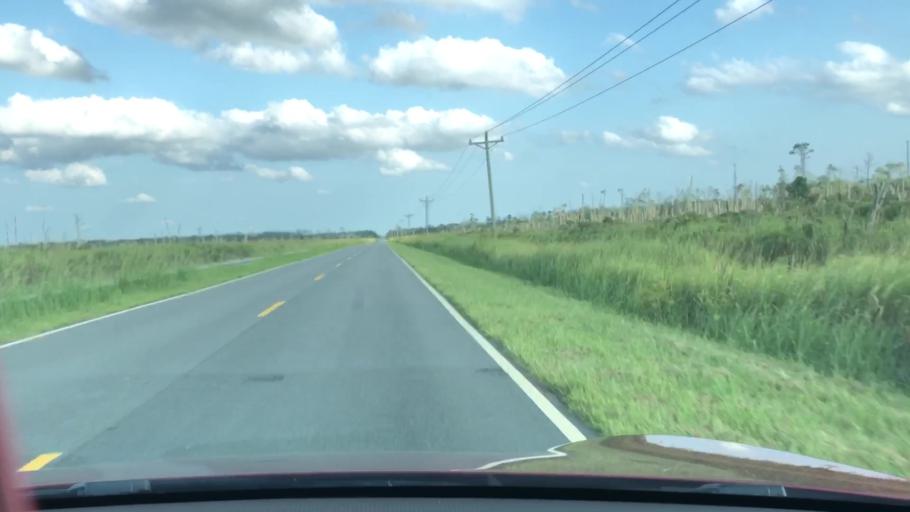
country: US
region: North Carolina
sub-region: Dare County
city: Wanchese
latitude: 35.6287
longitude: -75.8506
